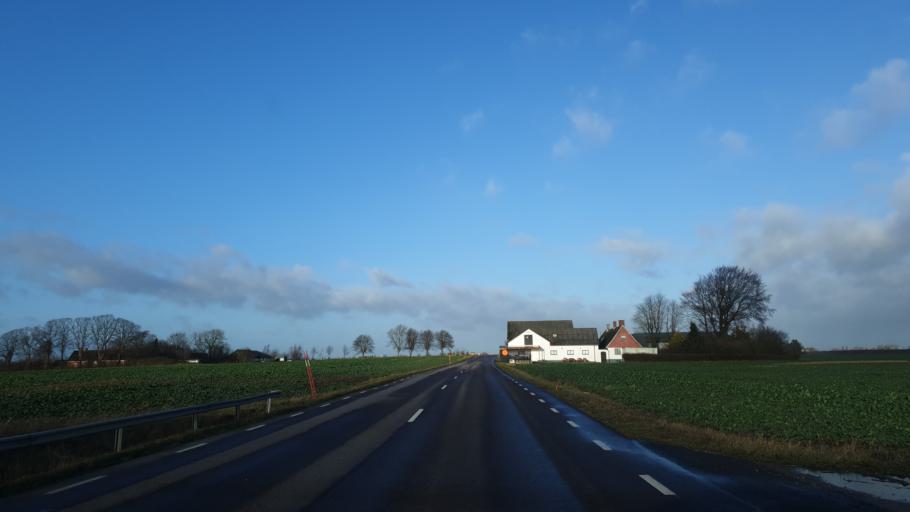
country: SE
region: Skane
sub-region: Vellinge Kommun
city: Vellinge
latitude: 55.4856
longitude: 13.0252
